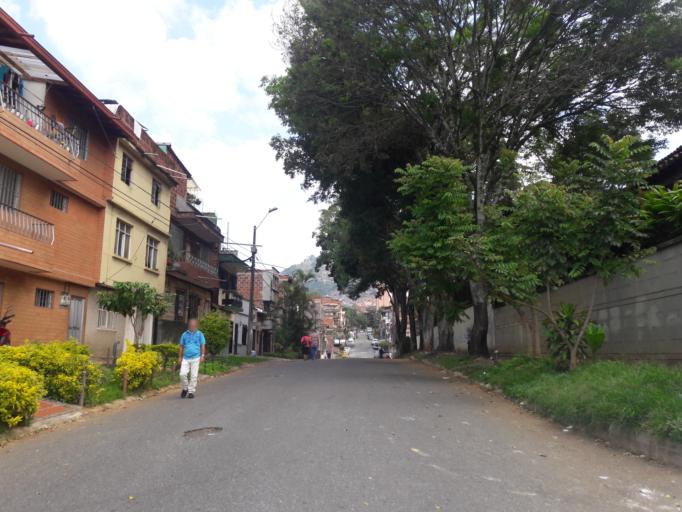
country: CO
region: Antioquia
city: Medellin
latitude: 6.2560
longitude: -75.5533
